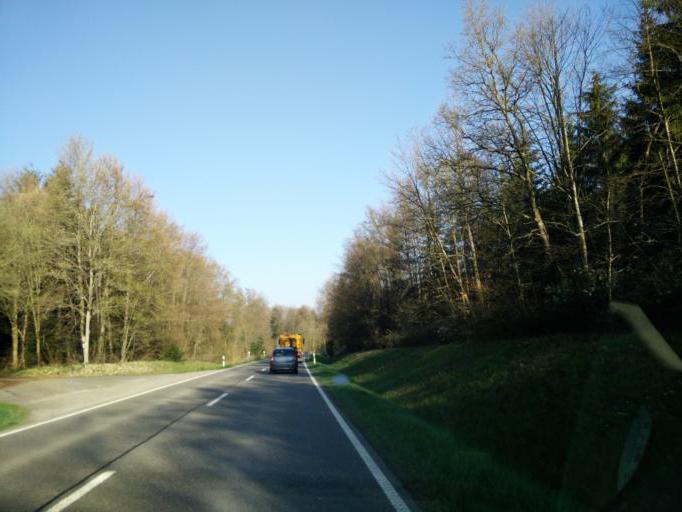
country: DE
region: Baden-Wuerttemberg
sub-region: Regierungsbezirk Stuttgart
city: Deckenpfronn
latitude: 48.6755
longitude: 8.7812
